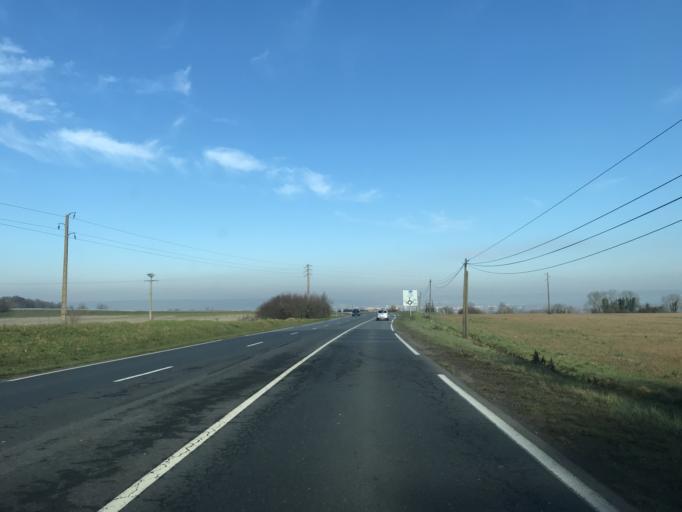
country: FR
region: Haute-Normandie
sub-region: Departement de l'Eure
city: Saint-Pierre-du-Vauvray
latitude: 49.2237
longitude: 1.2128
